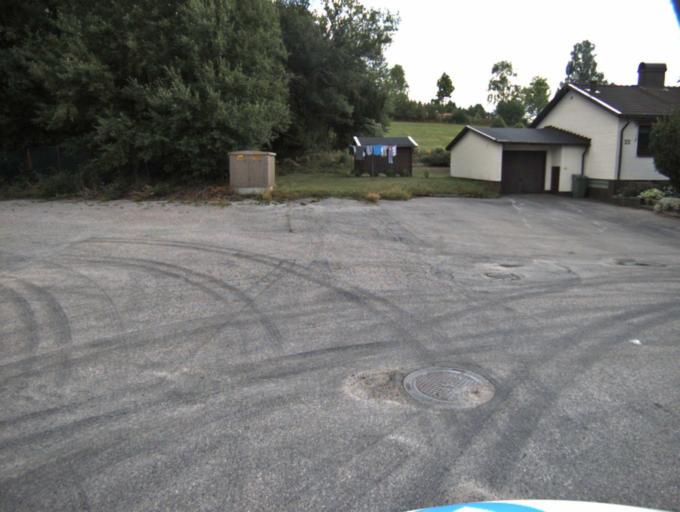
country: SE
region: Vaestra Goetaland
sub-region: Ulricehamns Kommun
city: Ulricehamn
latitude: 57.7017
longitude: 13.4998
